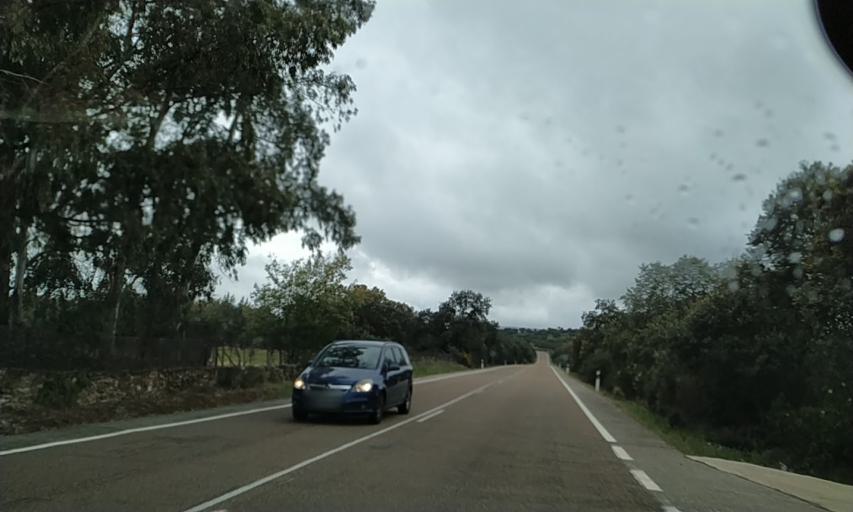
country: ES
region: Extremadura
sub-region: Provincia de Badajoz
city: Puebla de Obando
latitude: 39.2533
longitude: -6.5556
